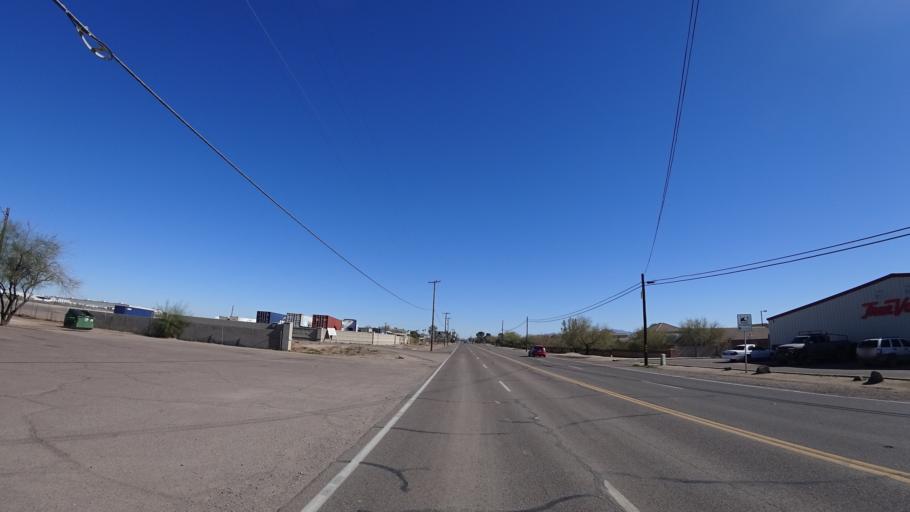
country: US
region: Arizona
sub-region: Maricopa County
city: Buckeye
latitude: 33.3777
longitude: -112.5682
